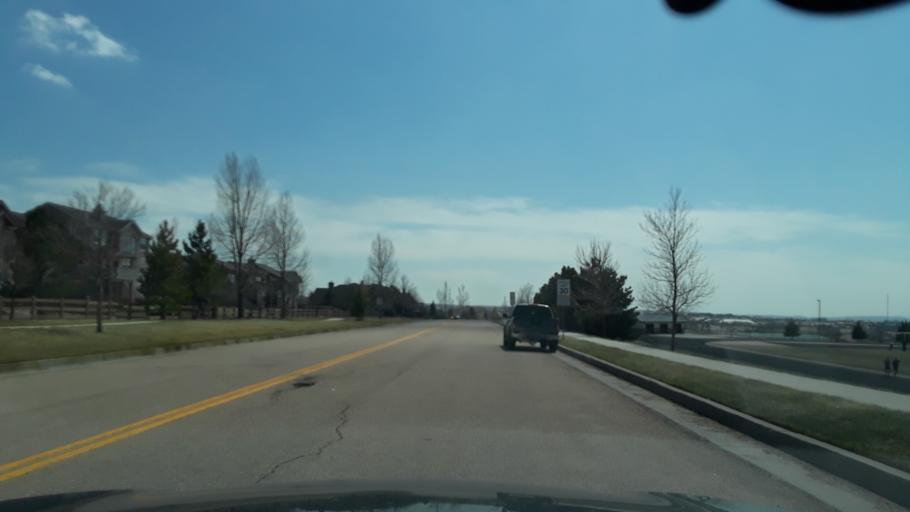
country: US
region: Colorado
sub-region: El Paso County
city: Gleneagle
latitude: 39.0335
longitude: -104.7915
